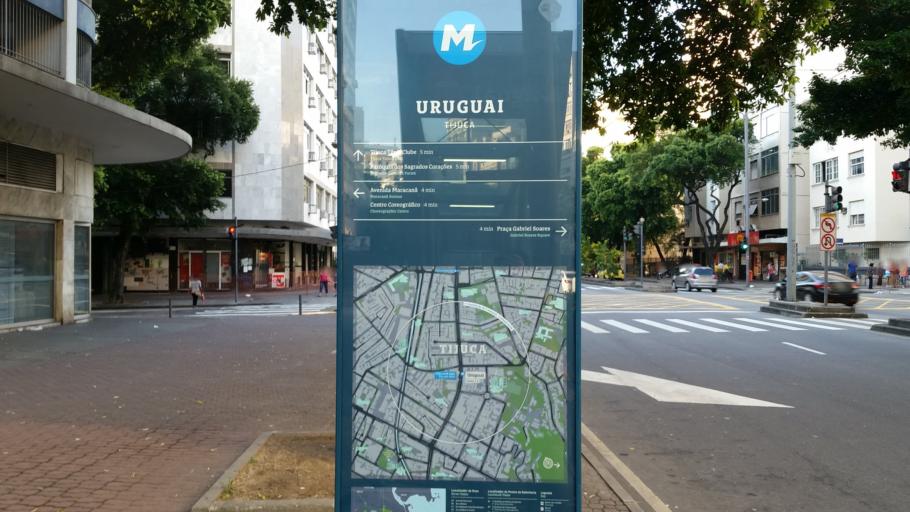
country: BR
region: Rio de Janeiro
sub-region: Rio De Janeiro
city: Rio de Janeiro
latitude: -22.9301
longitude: -43.2376
